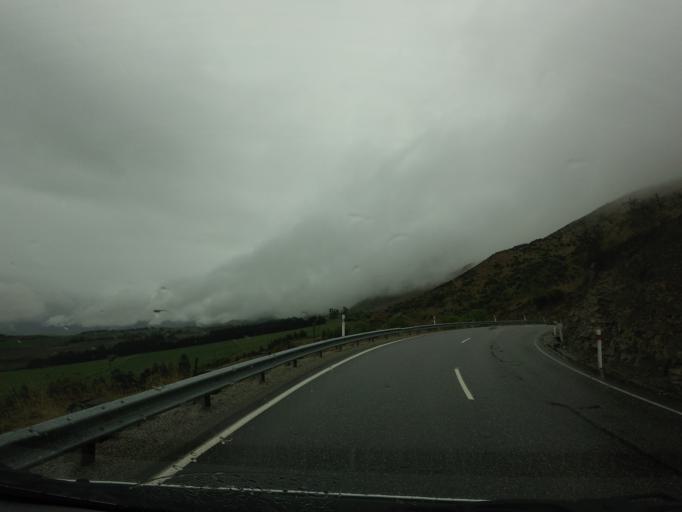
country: NZ
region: Otago
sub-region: Queenstown-Lakes District
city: Arrowtown
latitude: -44.9897
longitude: 168.9044
